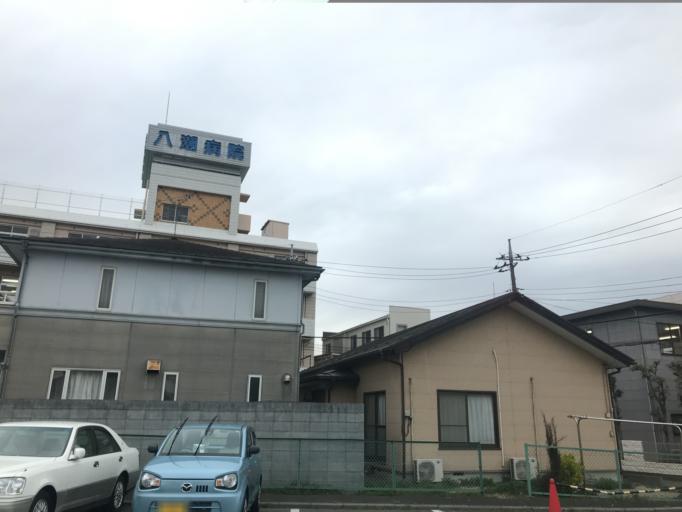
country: JP
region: Saitama
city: Yashio-shi
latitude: 35.8291
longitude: 139.8363
